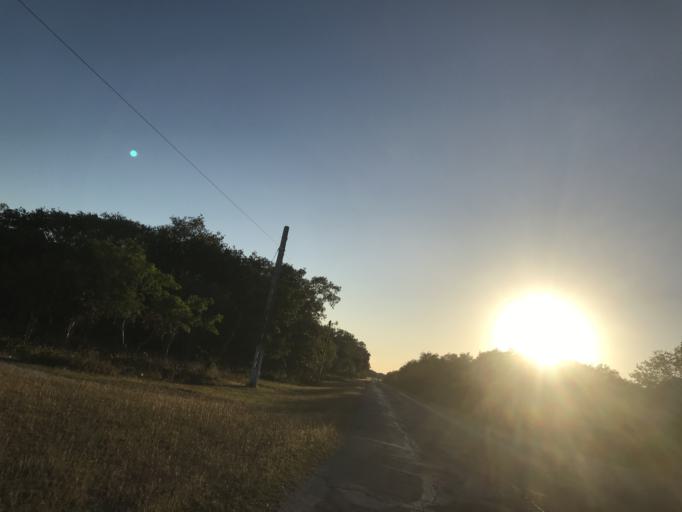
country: CU
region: Cienfuegos
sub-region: Municipio de Aguada de Pasajeros
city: Aguada de Pasajeros
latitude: 22.0718
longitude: -81.0357
